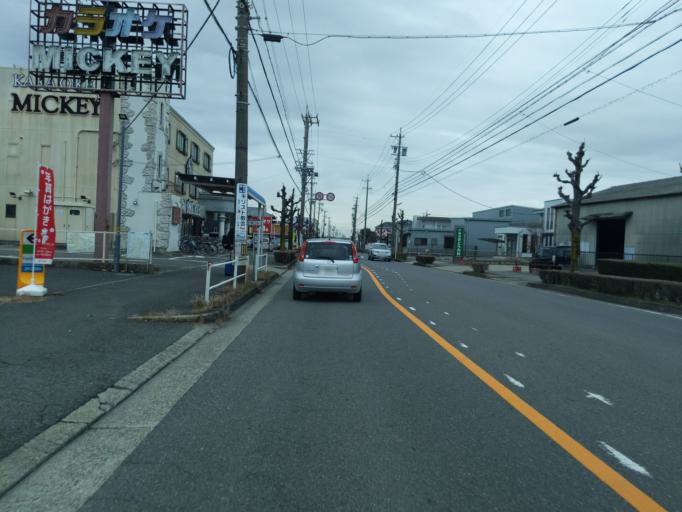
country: JP
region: Aichi
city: Kasugai
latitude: 35.2562
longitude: 136.9535
